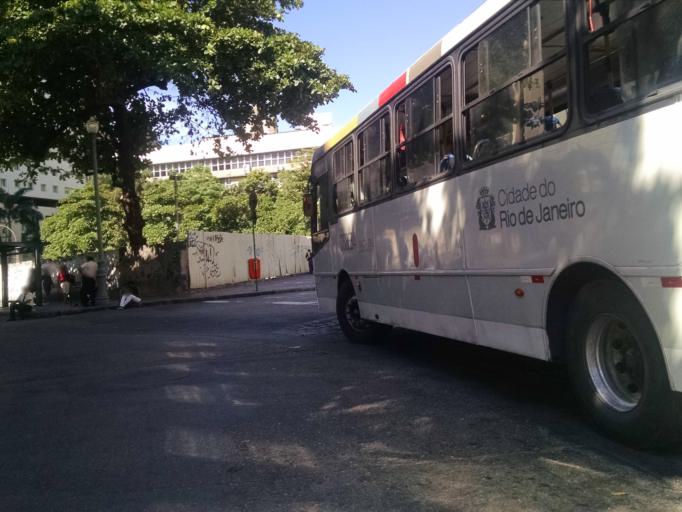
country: BR
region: Rio de Janeiro
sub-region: Rio De Janeiro
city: Rio de Janeiro
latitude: -22.9088
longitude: -43.1826
